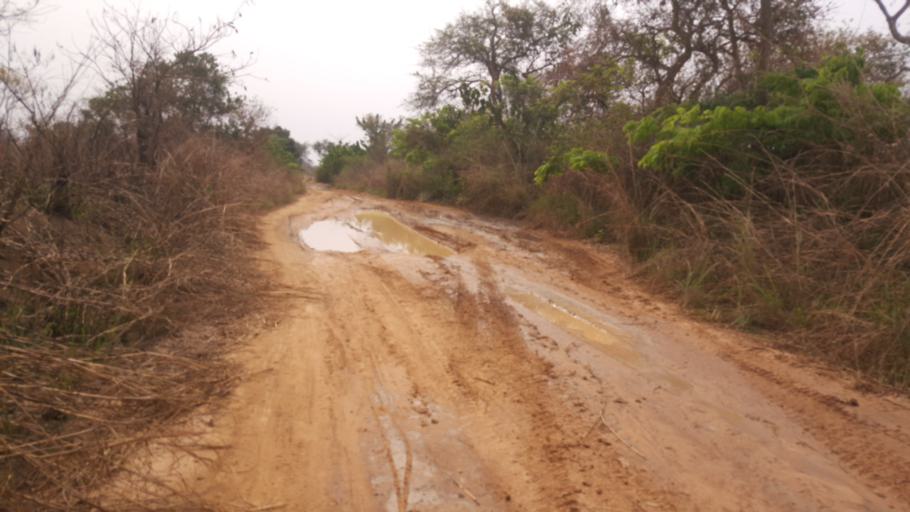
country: CD
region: Bandundu
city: Bandundu
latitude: -3.4540
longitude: 17.7484
